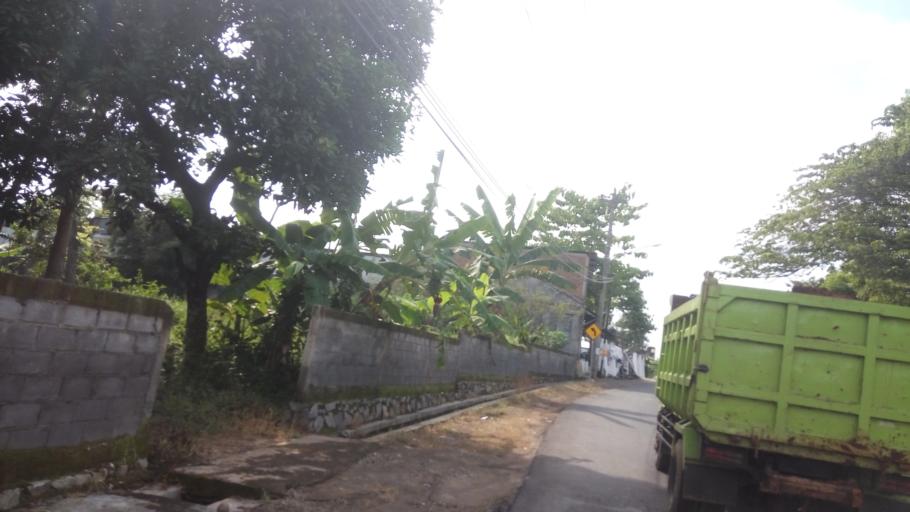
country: ID
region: Central Java
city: Ungaran
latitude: -7.1298
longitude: 110.4150
